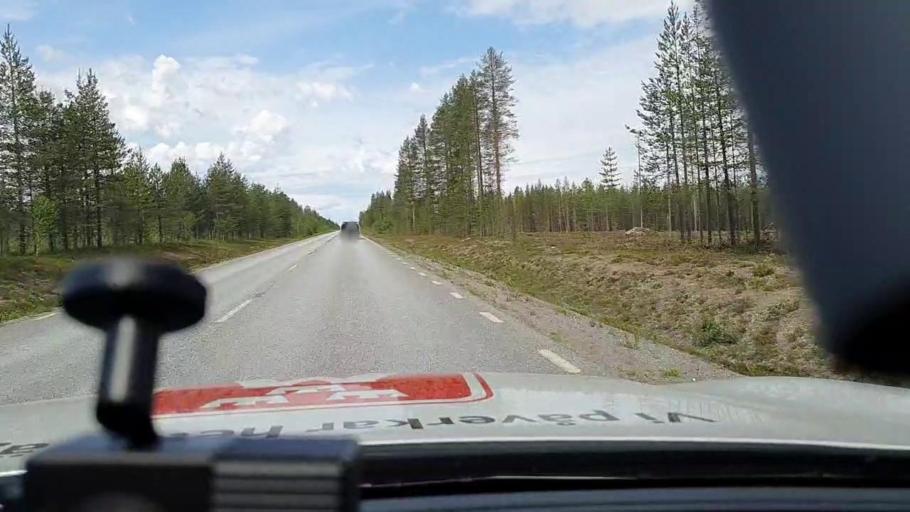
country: SE
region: Norrbotten
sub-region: Jokkmokks Kommun
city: Jokkmokk
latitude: 66.5210
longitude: 20.2129
